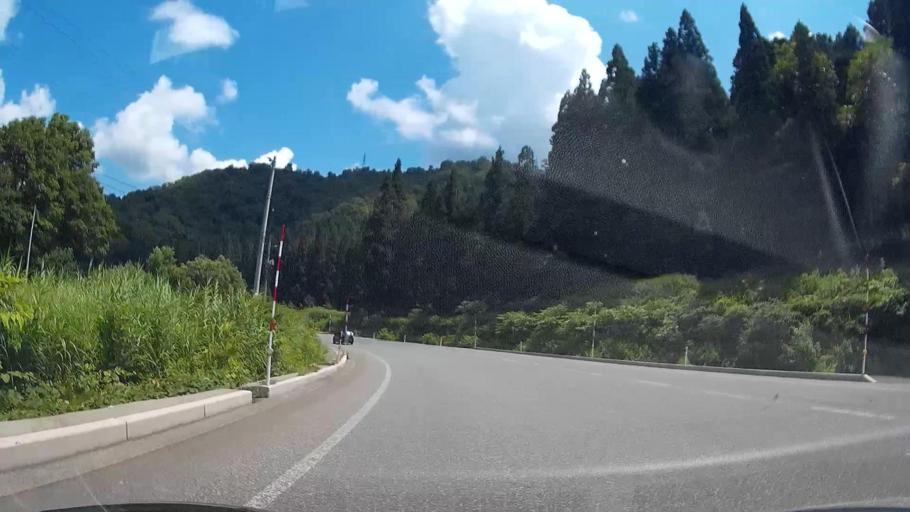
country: JP
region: Niigata
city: Shiozawa
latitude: 36.9087
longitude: 138.7977
